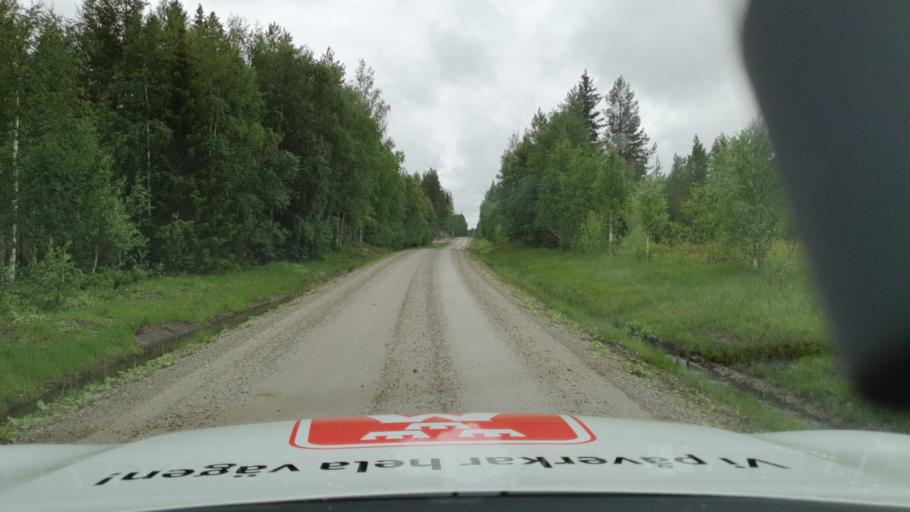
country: SE
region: Vaesterbotten
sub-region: Dorotea Kommun
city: Dorotea
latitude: 63.9995
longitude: 16.7992
